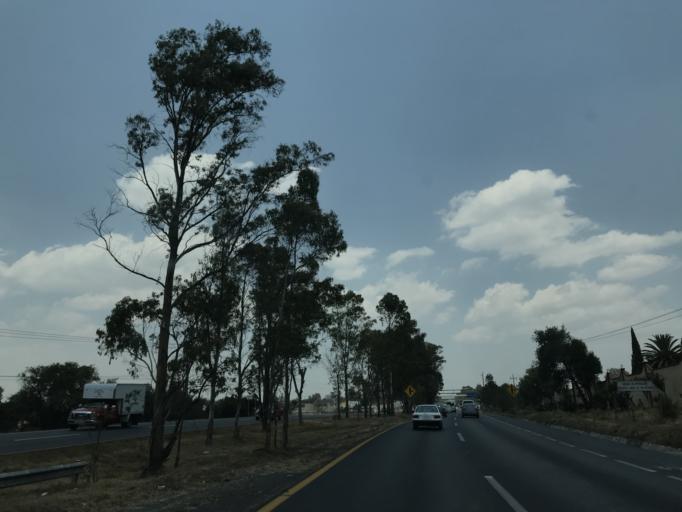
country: MX
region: Tlaxcala
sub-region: Yauhquemehcan
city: San Francisco Tlacuilohcan
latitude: 19.3836
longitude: -98.1784
